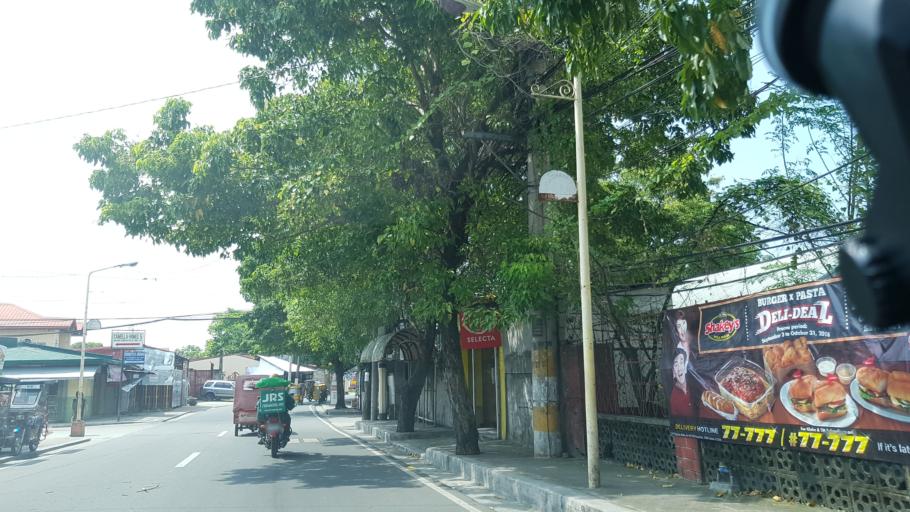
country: PH
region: Calabarzon
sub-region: Province of Rizal
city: Las Pinas
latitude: 14.4654
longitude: 120.9837
